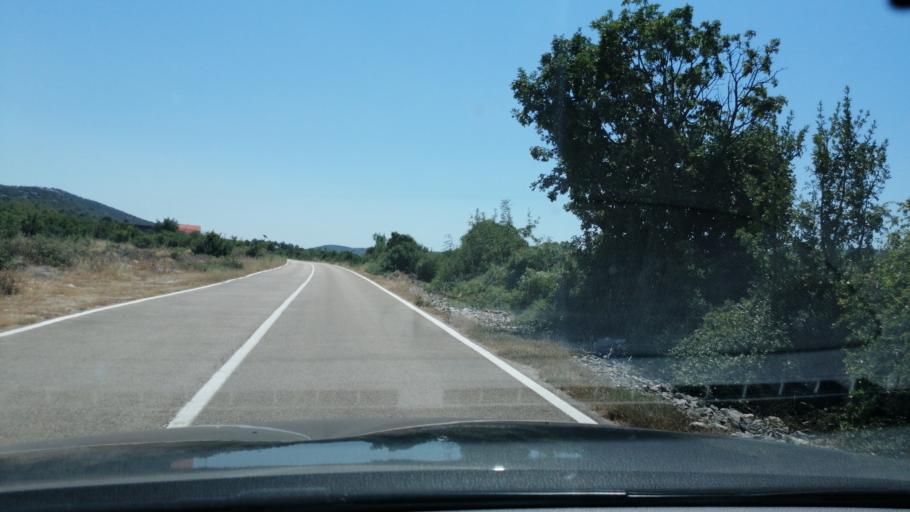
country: HR
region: Sibensko-Kniniska
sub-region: Grad Sibenik
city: Pirovac
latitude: 43.8800
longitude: 15.6757
